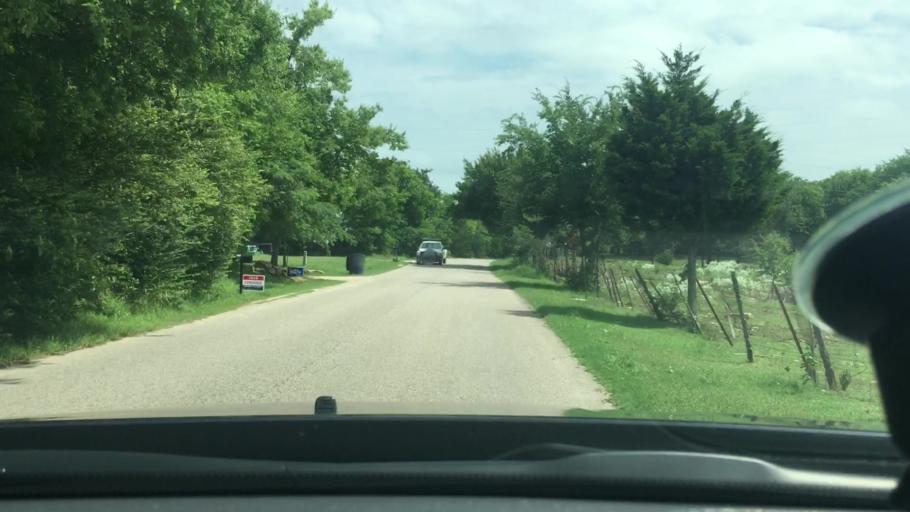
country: US
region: Oklahoma
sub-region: Pontotoc County
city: Ada
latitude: 34.8057
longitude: -96.6983
